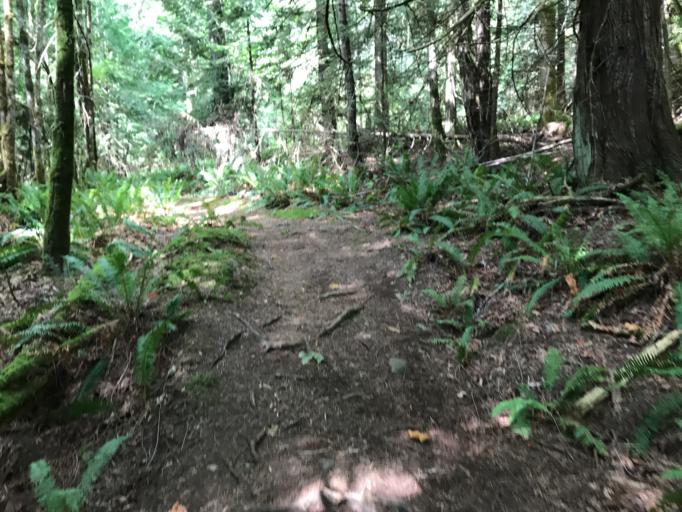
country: CA
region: British Columbia
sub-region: Cowichan Valley Regional District
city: Ladysmith
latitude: 48.9273
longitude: -123.7411
